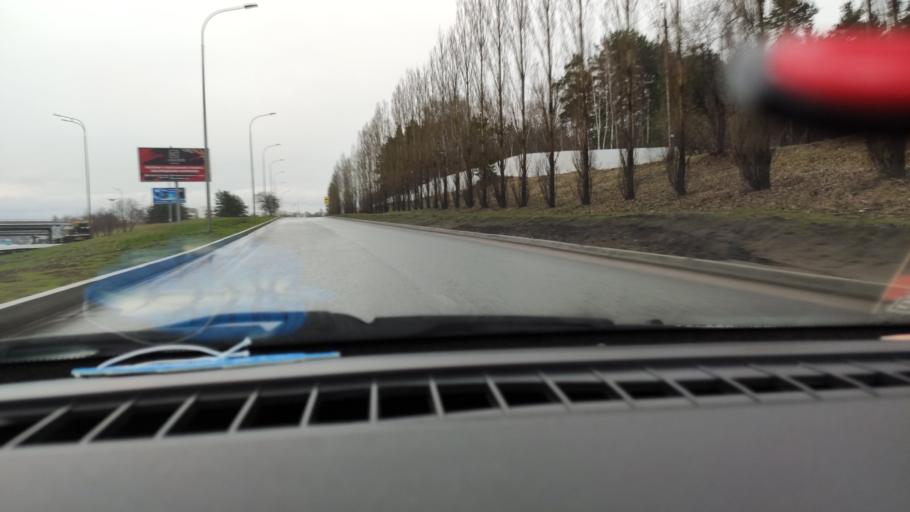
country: RU
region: Tatarstan
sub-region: Tukayevskiy Rayon
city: Naberezhnyye Chelny
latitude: 55.6752
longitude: 52.2832
